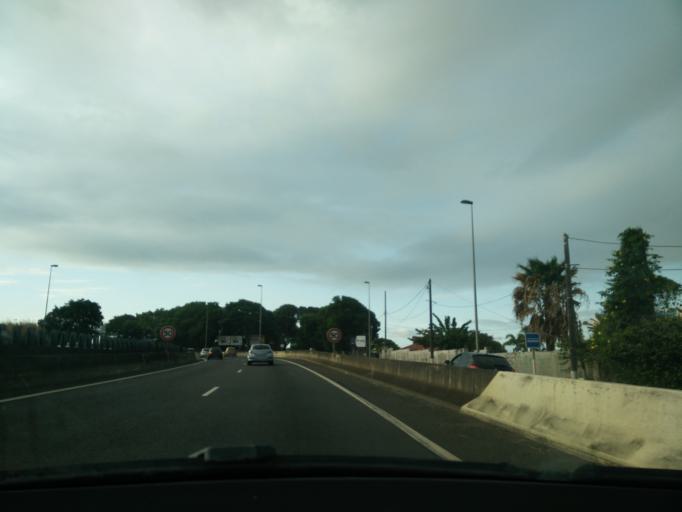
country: GP
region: Guadeloupe
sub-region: Guadeloupe
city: Baie-Mahault
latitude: 16.2457
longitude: -61.5881
